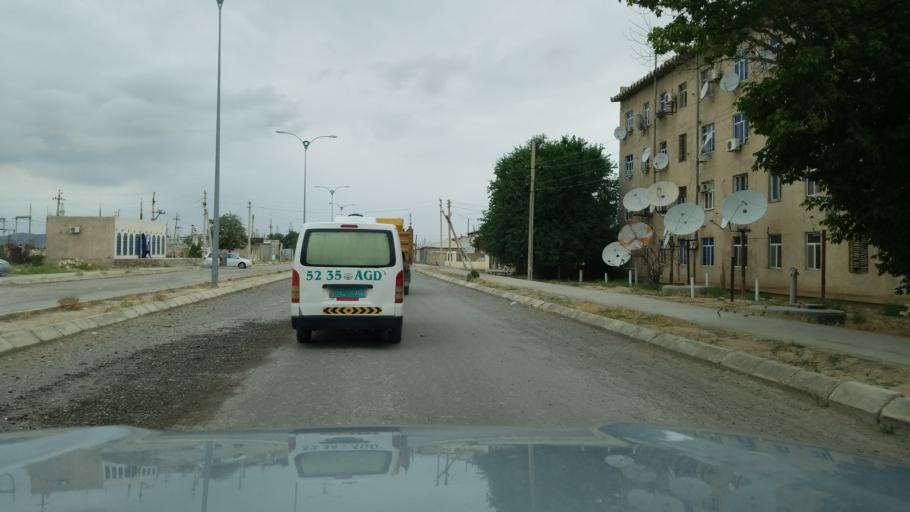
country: TM
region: Balkan
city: Serdar
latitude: 38.9711
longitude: 56.2601
